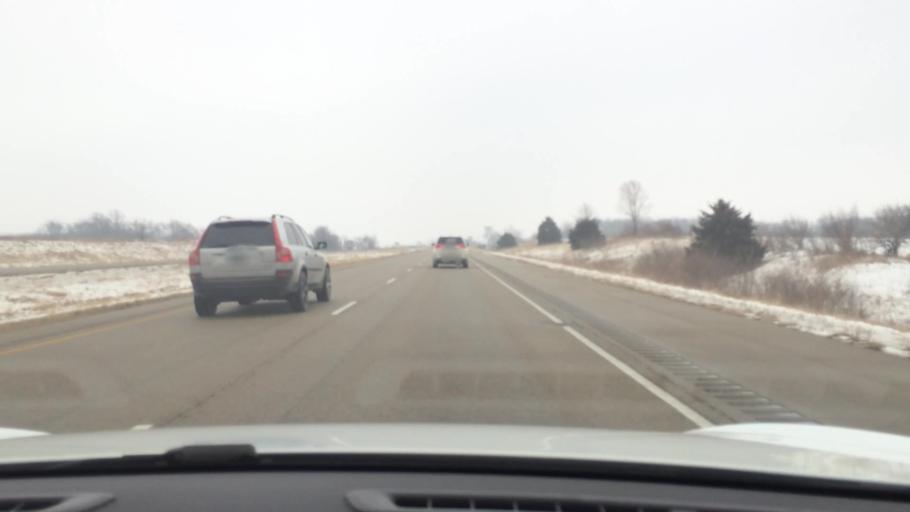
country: US
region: Illinois
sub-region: McLean County
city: Le Roy
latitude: 40.3308
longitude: -88.7500
